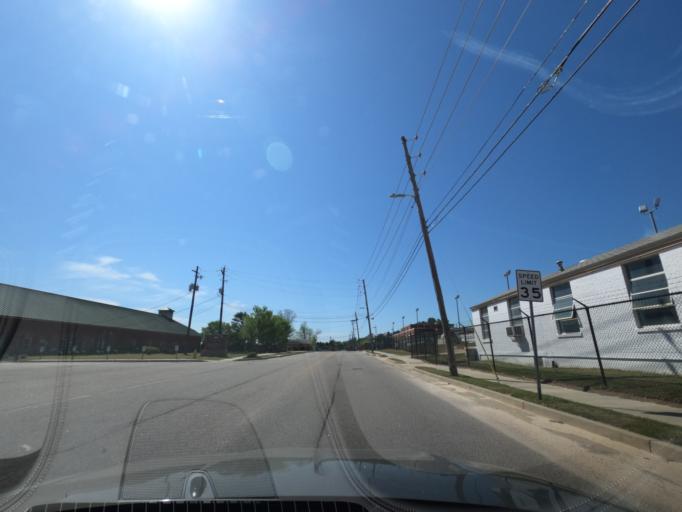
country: US
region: Georgia
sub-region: Richmond County
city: Augusta
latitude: 33.4710
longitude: -82.0326
